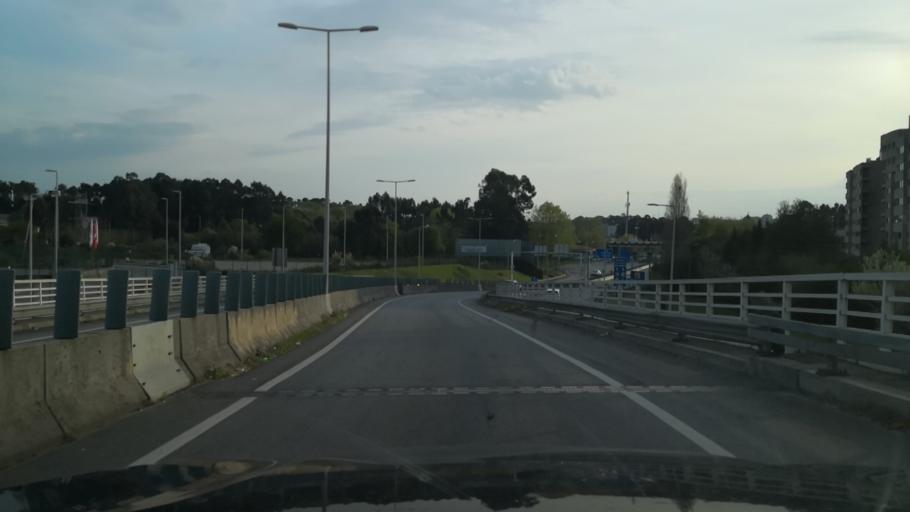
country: PT
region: Porto
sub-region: Gondomar
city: Baguim do Monte
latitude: 41.2047
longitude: -8.5486
